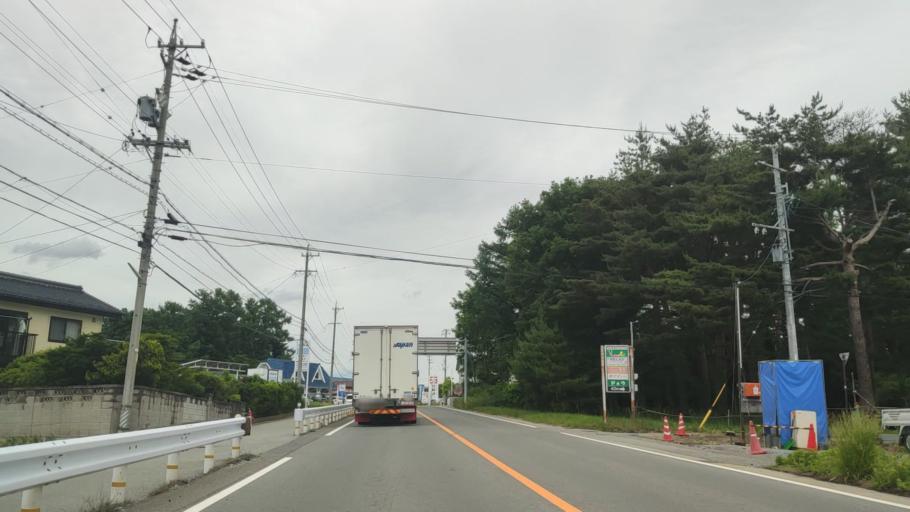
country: JP
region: Nagano
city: Komoro
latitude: 36.3228
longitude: 138.4998
